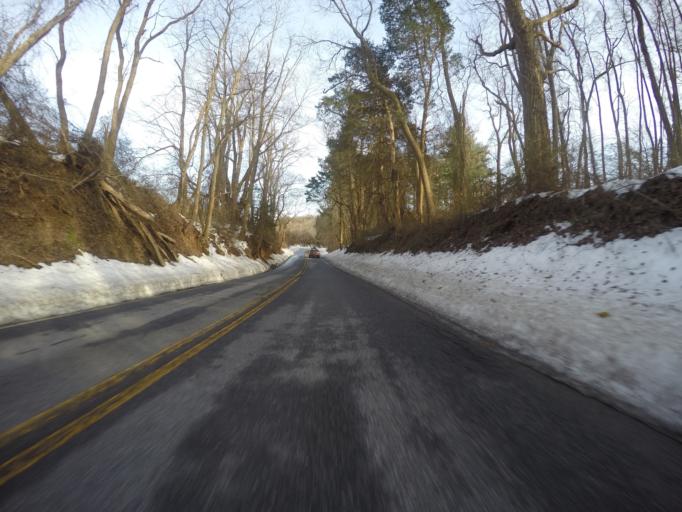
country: US
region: Maryland
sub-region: Harford County
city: Jarrettsville
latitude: 39.5398
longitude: -76.5514
